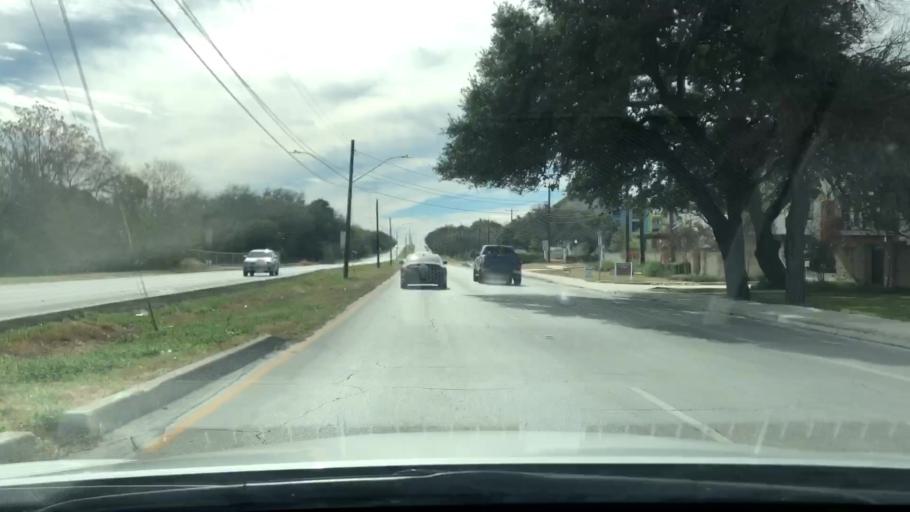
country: US
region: Texas
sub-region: Bexar County
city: Terrell Hills
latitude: 29.5053
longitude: -98.4348
